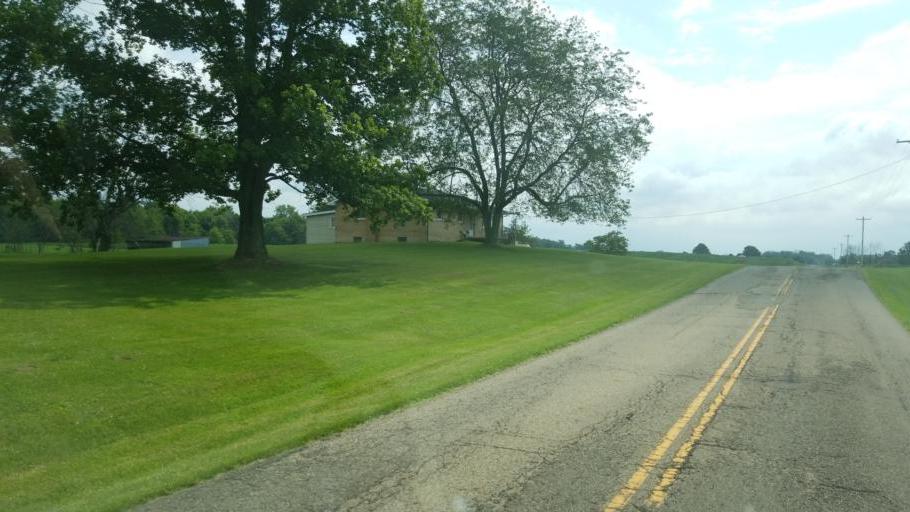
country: US
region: Ohio
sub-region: Knox County
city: Centerburg
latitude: 40.3180
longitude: -82.6066
